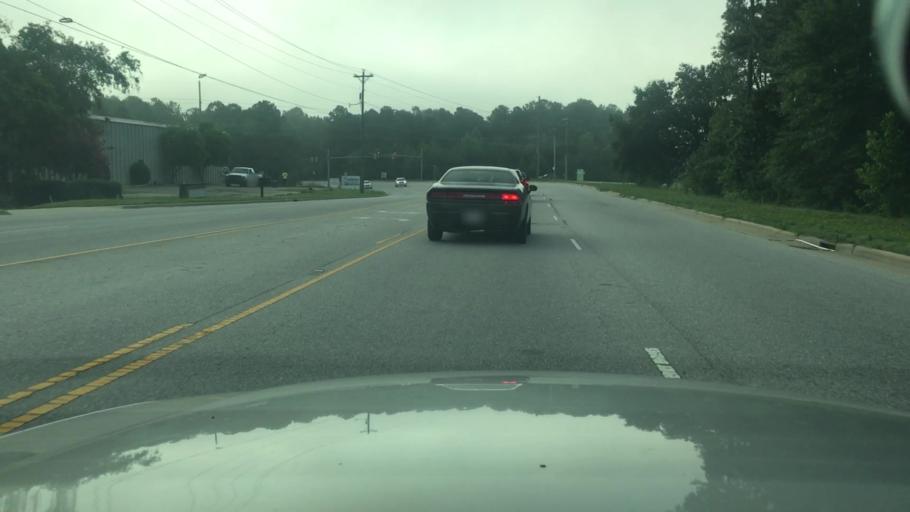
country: US
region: North Carolina
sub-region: Cumberland County
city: Hope Mills
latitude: 35.0010
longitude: -78.9068
